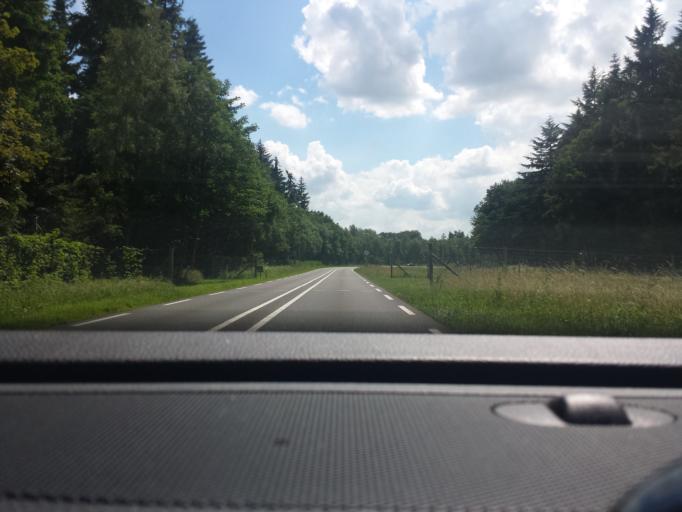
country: NL
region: Overijssel
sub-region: Gemeente Hof van Twente
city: Diepenheim
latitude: 52.2044
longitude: 6.5293
